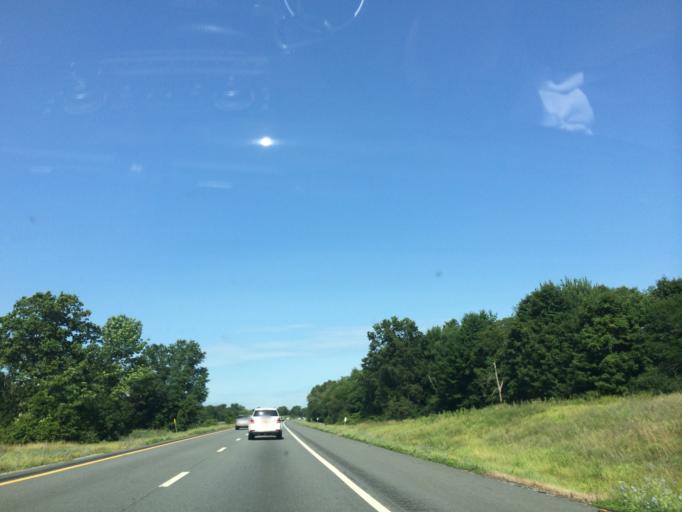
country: US
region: New York
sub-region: Orange County
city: Orange Lake
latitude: 41.5123
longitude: -74.1443
